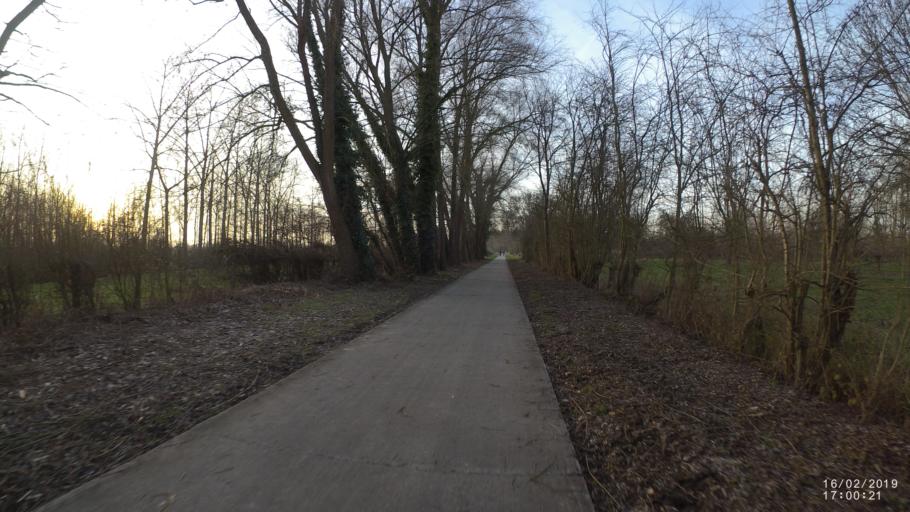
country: BE
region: Flanders
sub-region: Provincie Vlaams-Brabant
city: Zoutleeuw
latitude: 50.8248
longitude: 5.1125
